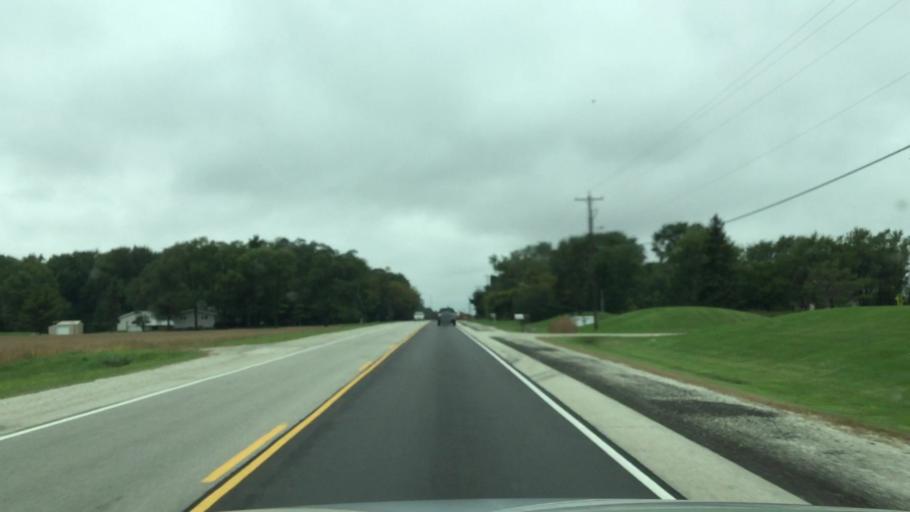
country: US
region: Wisconsin
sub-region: Racine County
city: Union Grove
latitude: 42.7422
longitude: -88.0781
